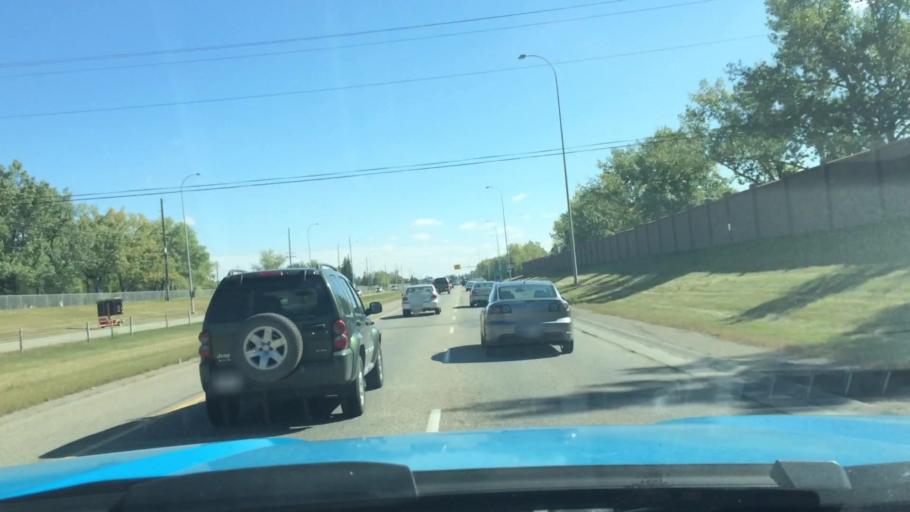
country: CA
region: Alberta
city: Calgary
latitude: 50.9481
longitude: -114.0492
